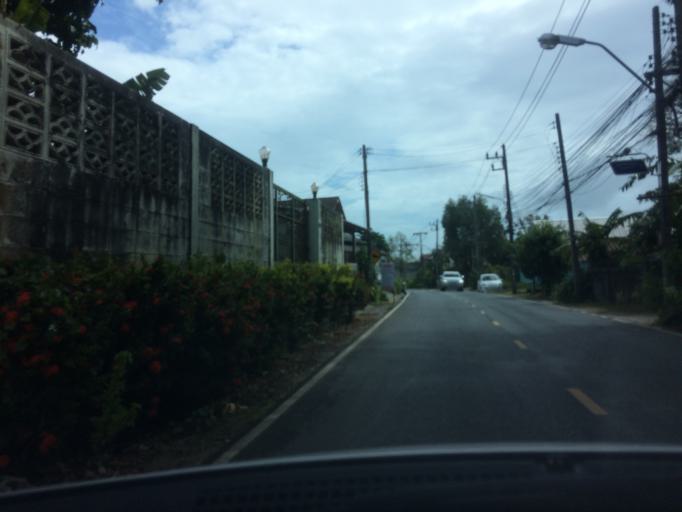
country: TH
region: Phuket
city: Thalang
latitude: 8.0281
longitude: 98.3365
